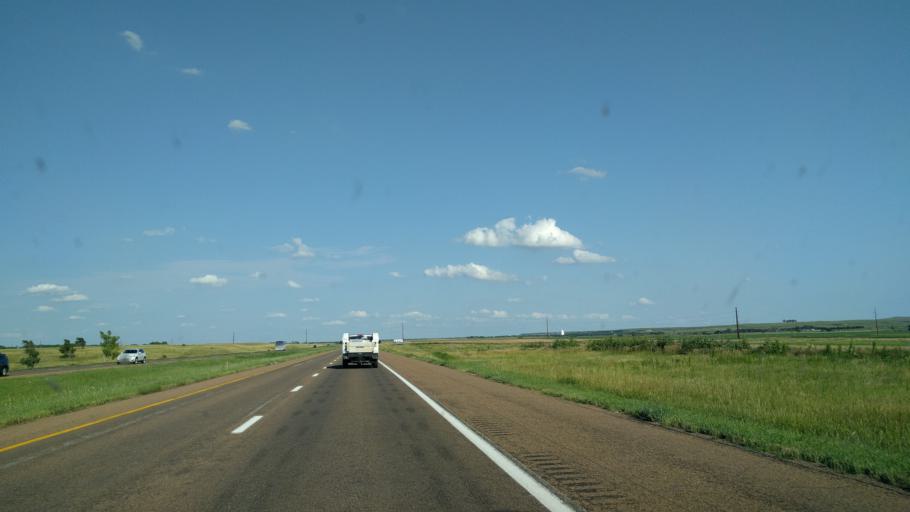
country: US
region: Kansas
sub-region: Ellis County
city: Ellis
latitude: 38.9353
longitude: -99.4729
